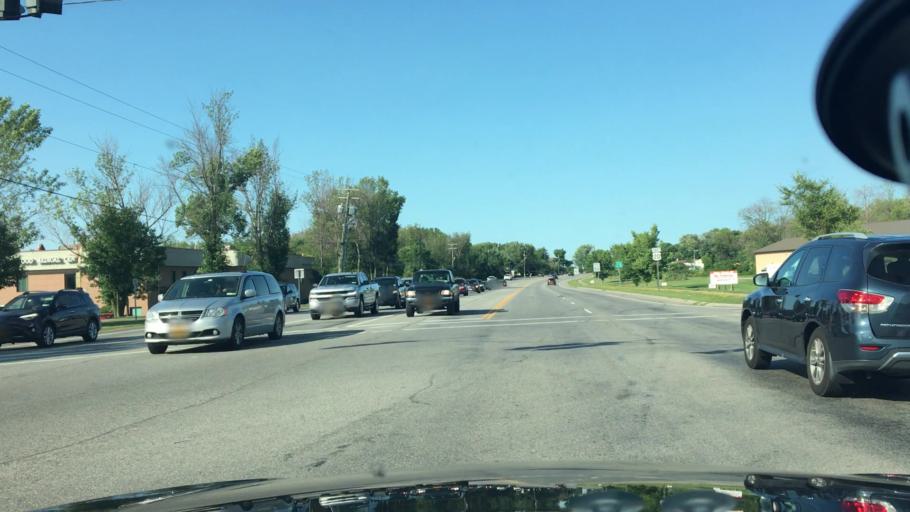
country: US
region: New York
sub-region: Erie County
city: Wanakah
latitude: 42.7356
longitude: -78.8794
